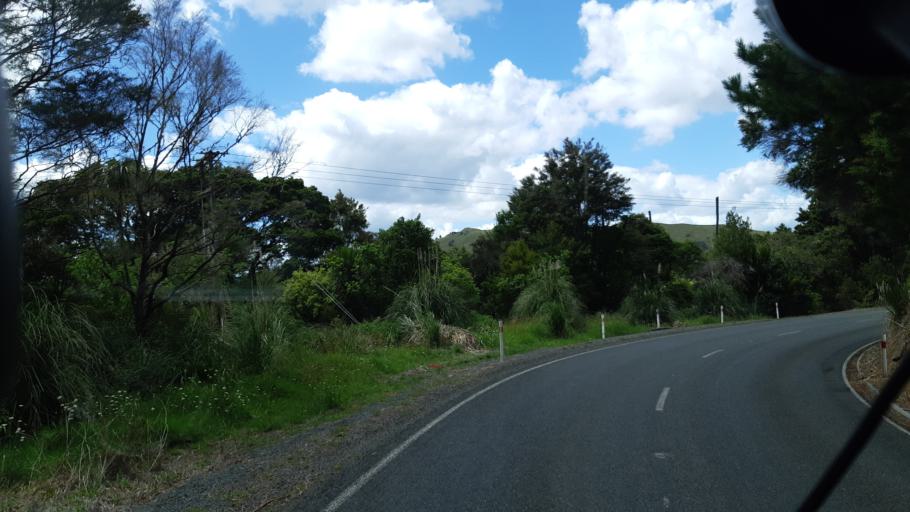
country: NZ
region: Northland
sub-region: Far North District
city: Taipa
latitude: -35.2543
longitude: 173.5345
